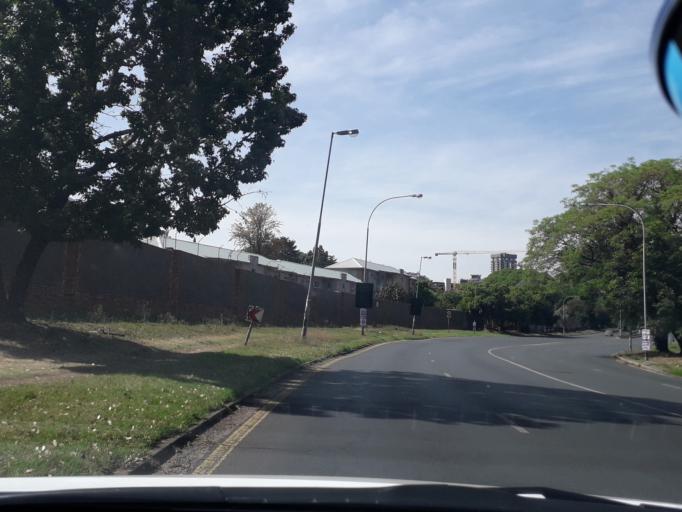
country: ZA
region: Gauteng
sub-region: City of Johannesburg Metropolitan Municipality
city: Johannesburg
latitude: -26.1738
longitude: 28.0170
